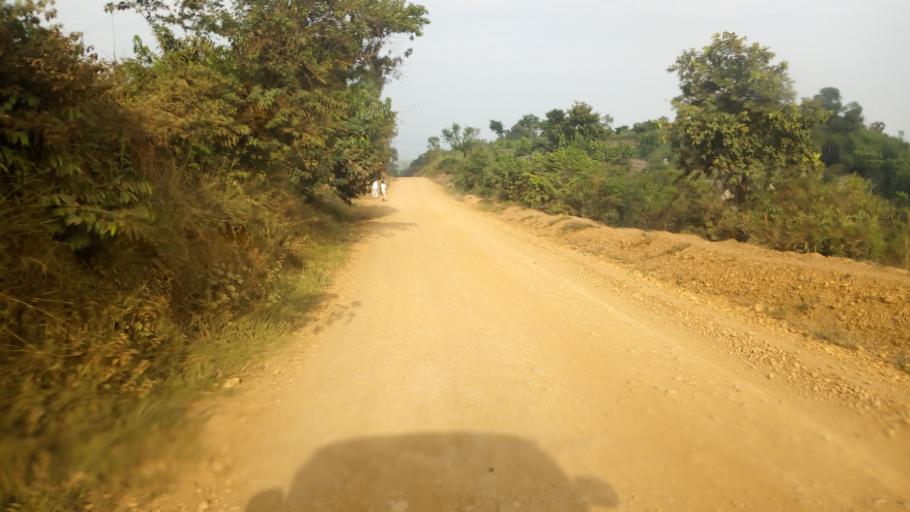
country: UG
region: Western Region
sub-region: Kanungu District
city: Ntungamo
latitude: -0.8332
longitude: 29.6914
